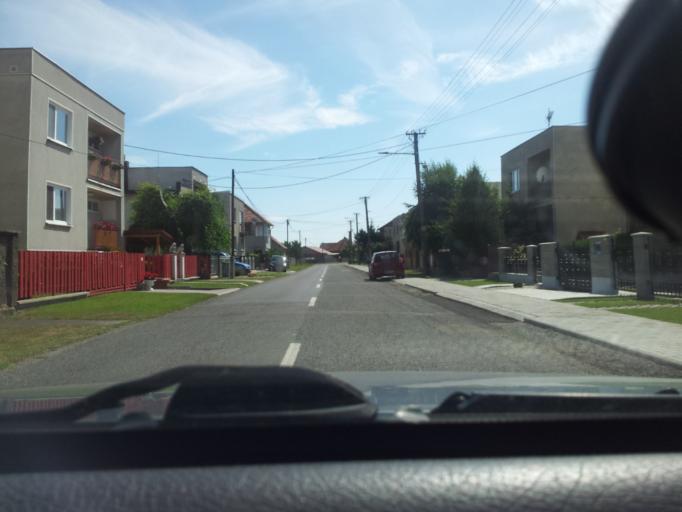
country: SK
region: Nitriansky
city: Tlmace
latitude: 48.2754
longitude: 18.5456
